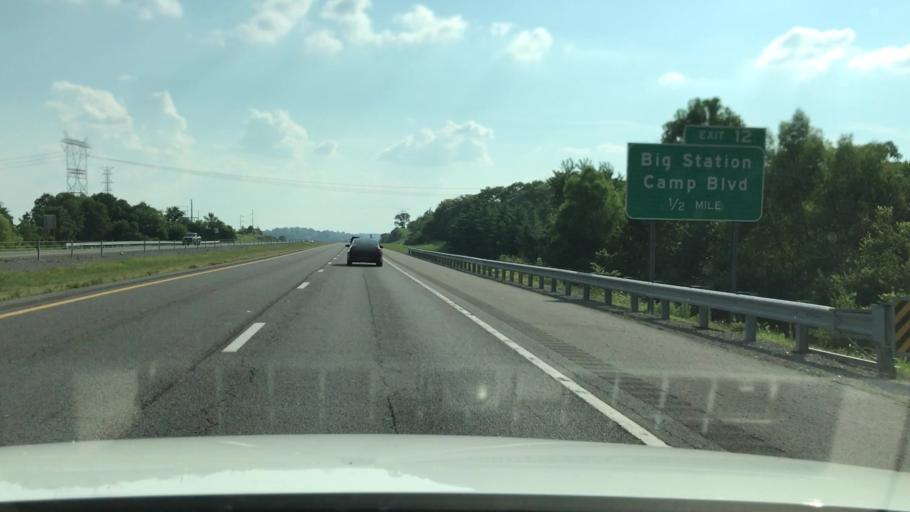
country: US
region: Tennessee
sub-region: Sumner County
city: Gallatin
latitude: 36.3645
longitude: -86.5232
